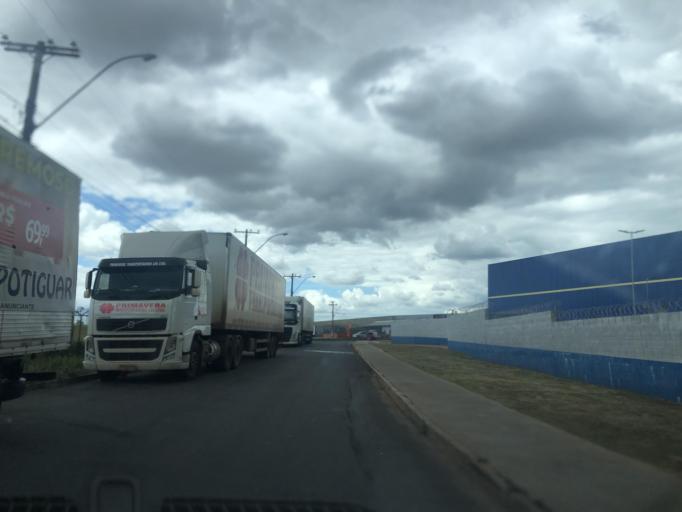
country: BR
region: Federal District
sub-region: Brasilia
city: Brasilia
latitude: -15.8738
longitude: -48.0263
